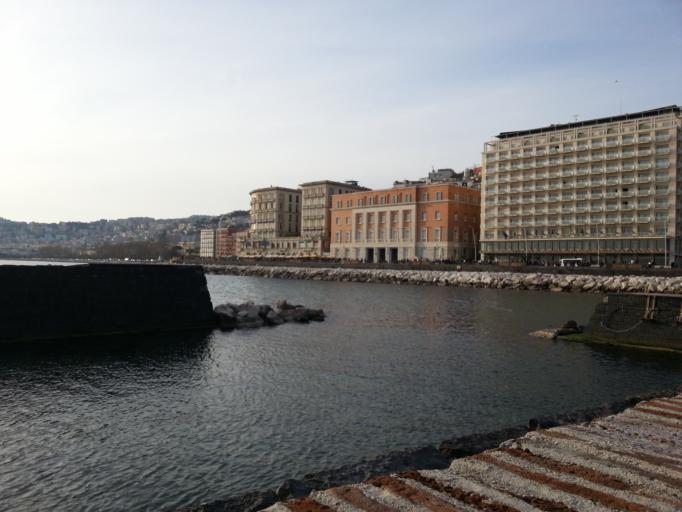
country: IT
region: Campania
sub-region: Provincia di Napoli
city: Napoli
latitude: 40.8286
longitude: 14.2475
